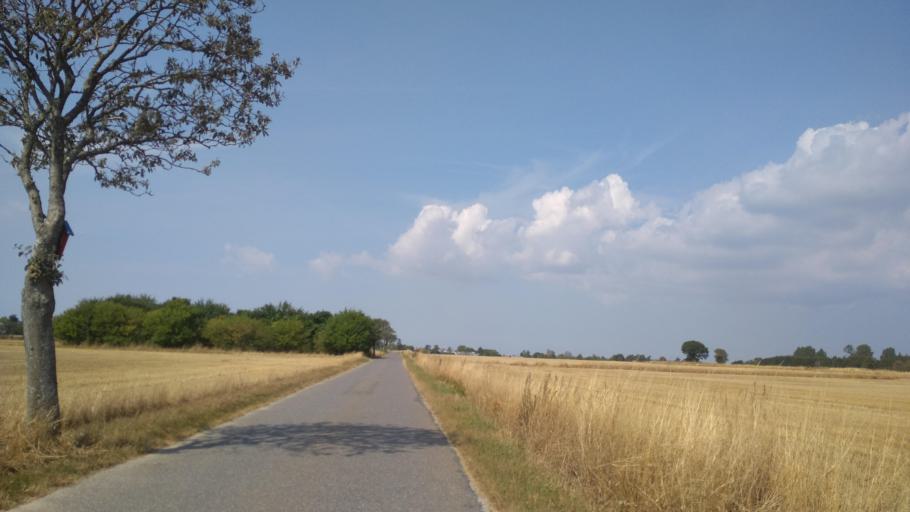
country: DK
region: Capital Region
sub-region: Bornholm Kommune
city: Akirkeby
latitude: 55.0642
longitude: 14.9366
